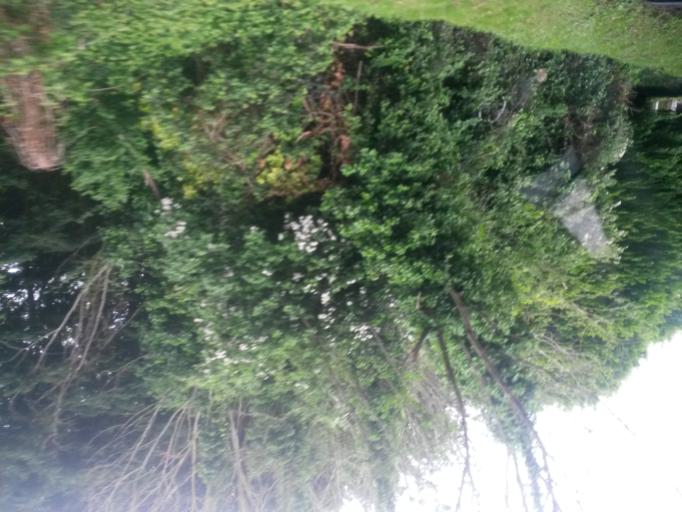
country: IE
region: Leinster
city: Donabate
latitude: 53.4943
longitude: -6.1917
